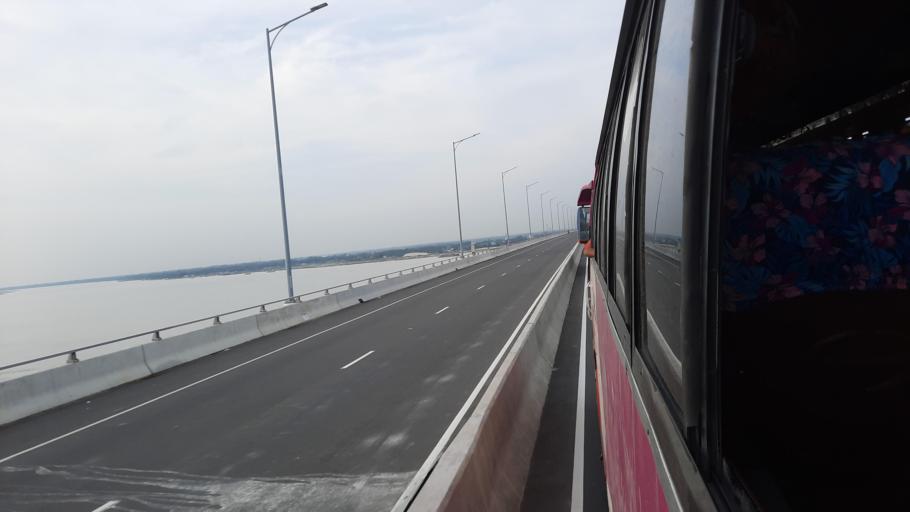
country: BD
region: Dhaka
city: Char Bhadrasan
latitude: 23.4567
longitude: 90.2619
